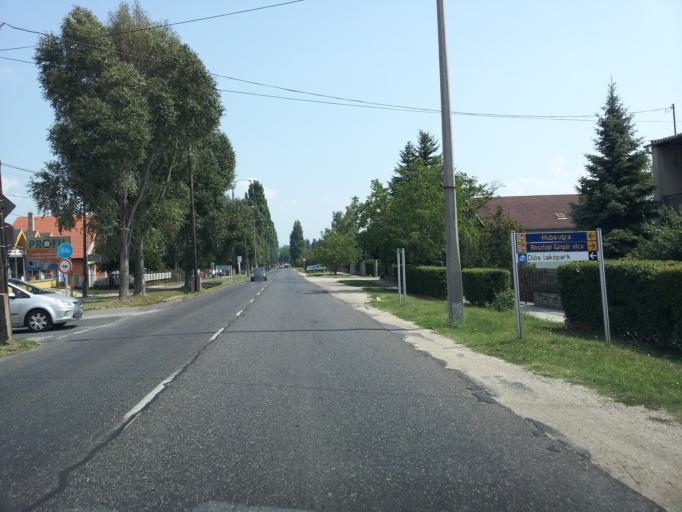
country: HU
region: Veszprem
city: Balatonalmadi
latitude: 47.0364
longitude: 18.0214
